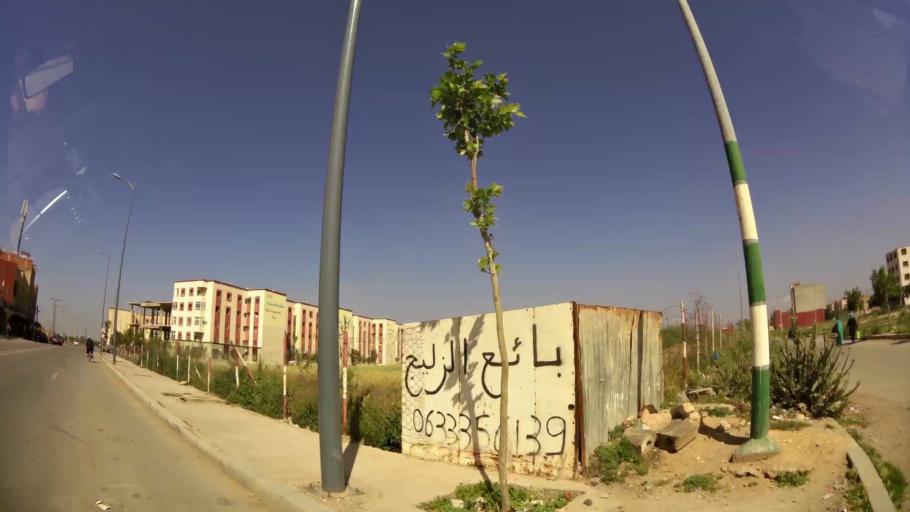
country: MA
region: Oriental
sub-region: Oujda-Angad
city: Oujda
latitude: 34.6984
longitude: -1.8775
